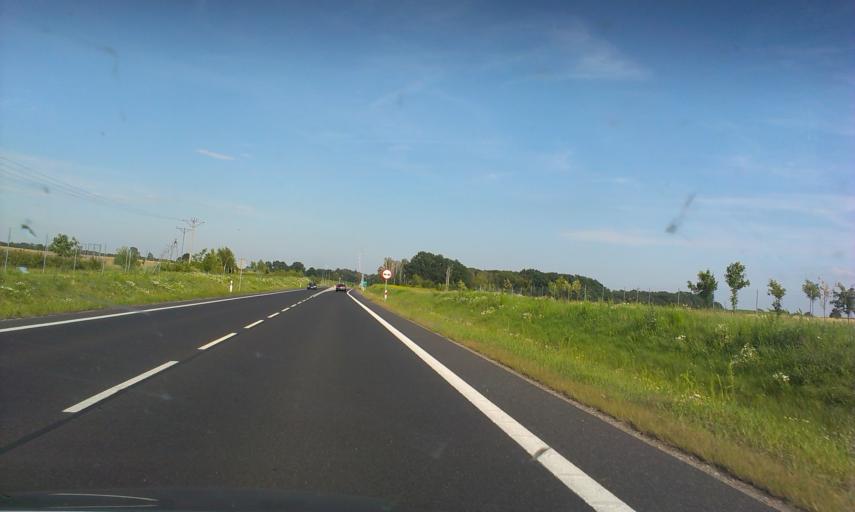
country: PL
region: Greater Poland Voivodeship
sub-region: Powiat pilski
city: Wyrzysk
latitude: 53.1607
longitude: 17.2888
